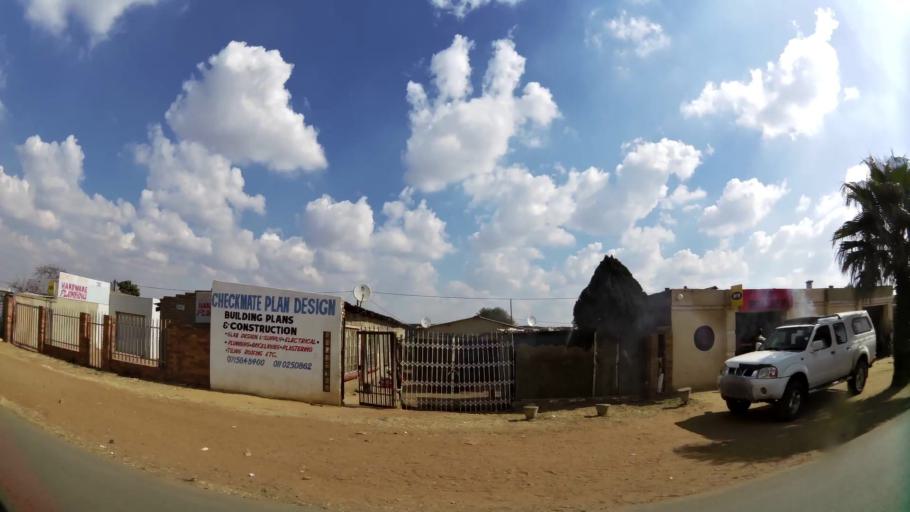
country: ZA
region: Gauteng
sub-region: City of Johannesburg Metropolitan Municipality
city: Roodepoort
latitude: -26.1938
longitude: 27.8682
